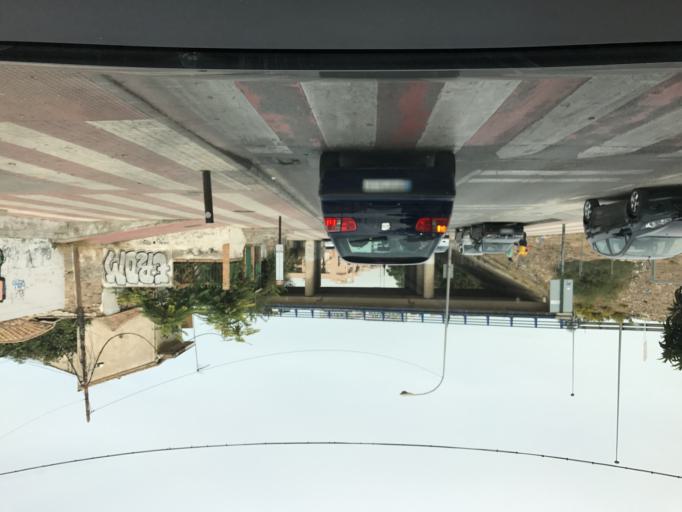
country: ES
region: Andalusia
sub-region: Provincia de Granada
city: Maracena
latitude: 37.2035
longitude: -3.6266
